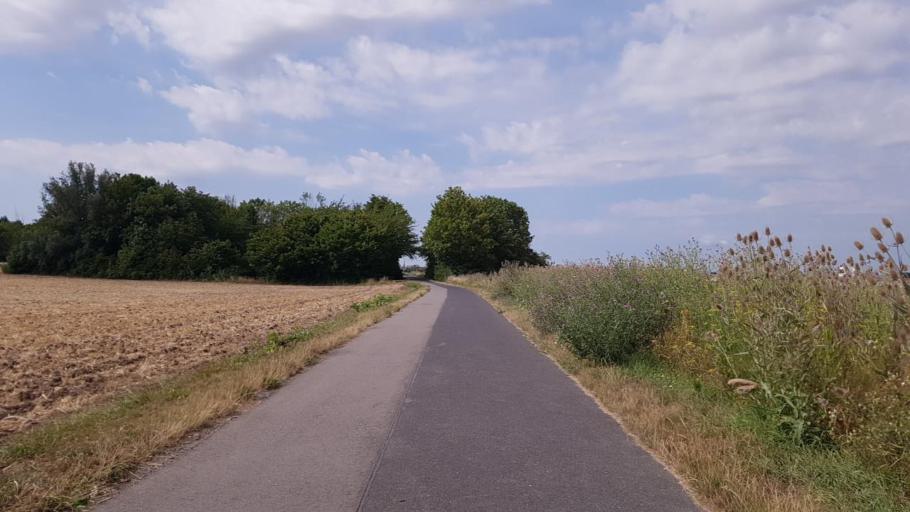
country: DE
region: Rheinland-Pfalz
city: Frankenthal
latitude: 49.5121
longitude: 8.3954
